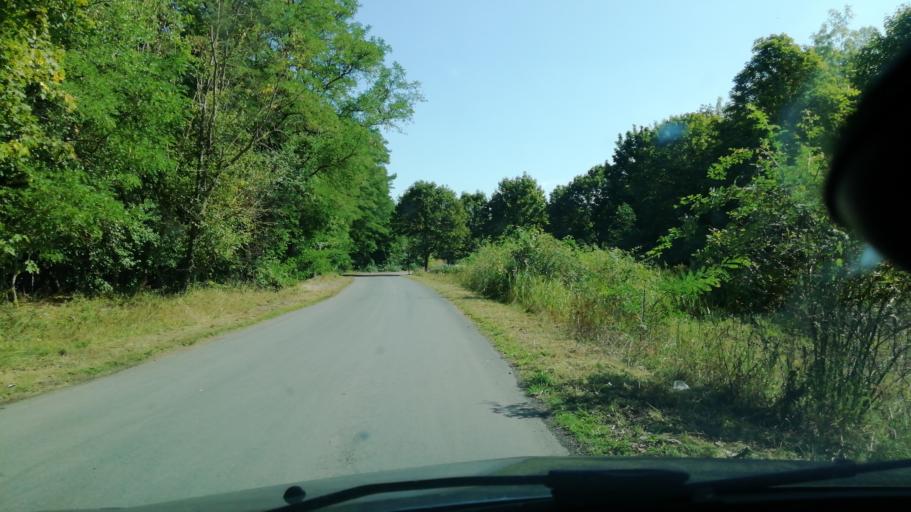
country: FR
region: Nord-Pas-de-Calais
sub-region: Departement du Nord
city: Conde-sur-l'Escaut
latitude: 50.4613
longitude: 3.6071
